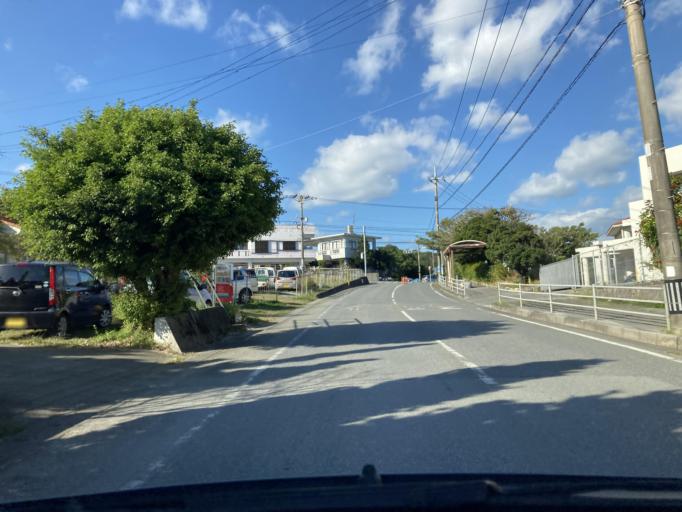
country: JP
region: Okinawa
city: Ginowan
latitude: 26.2195
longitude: 127.7543
